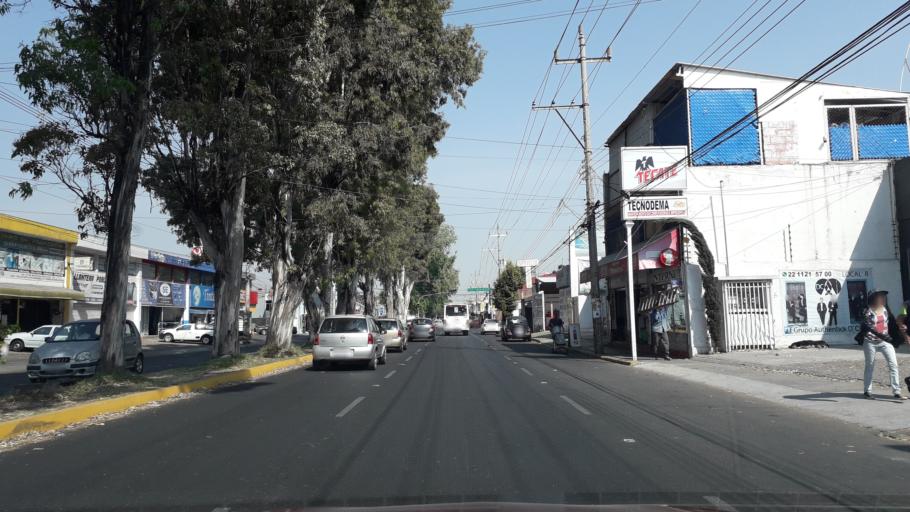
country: MX
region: Puebla
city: Puebla
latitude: 19.0672
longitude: -98.2169
